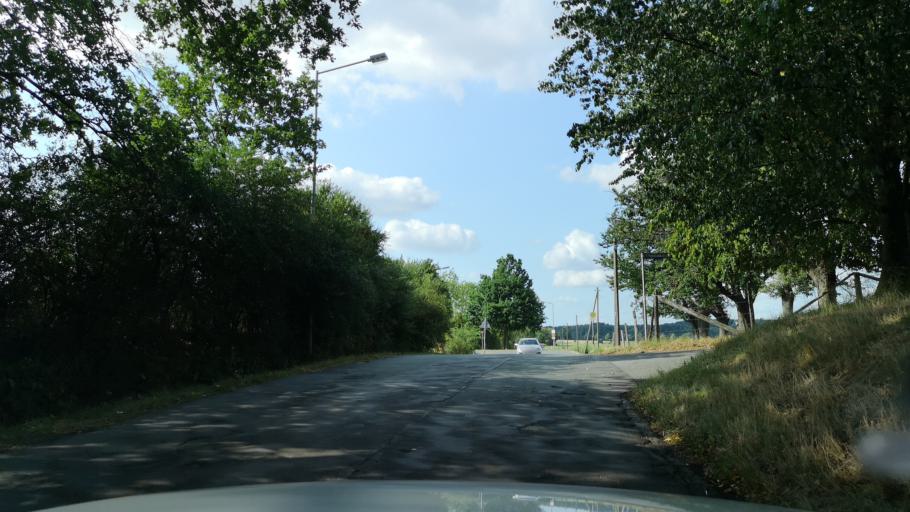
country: DE
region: North Rhine-Westphalia
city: Iserlohn
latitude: 51.4282
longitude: 7.7112
